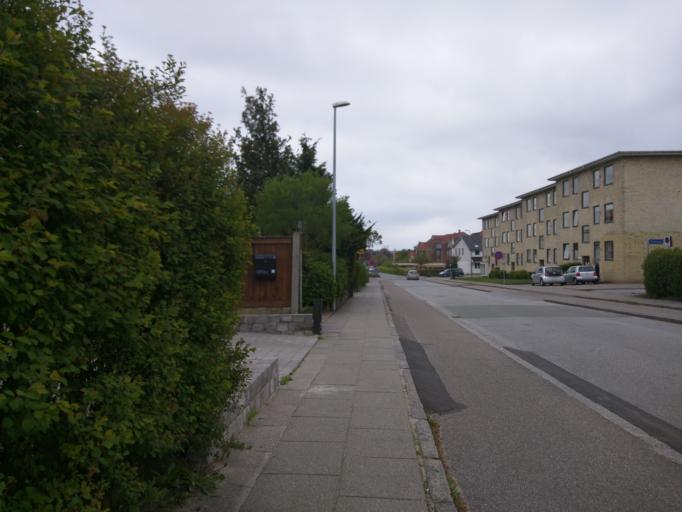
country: DK
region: Central Jutland
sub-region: Viborg Kommune
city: Viborg
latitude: 56.4510
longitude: 9.3981
